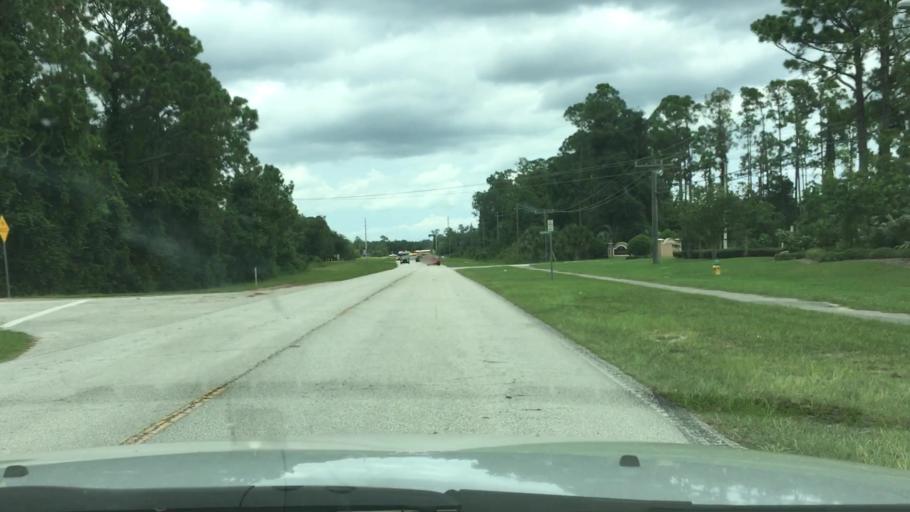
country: US
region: Florida
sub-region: Volusia County
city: Holly Hill
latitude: 29.2292
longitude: -81.0702
